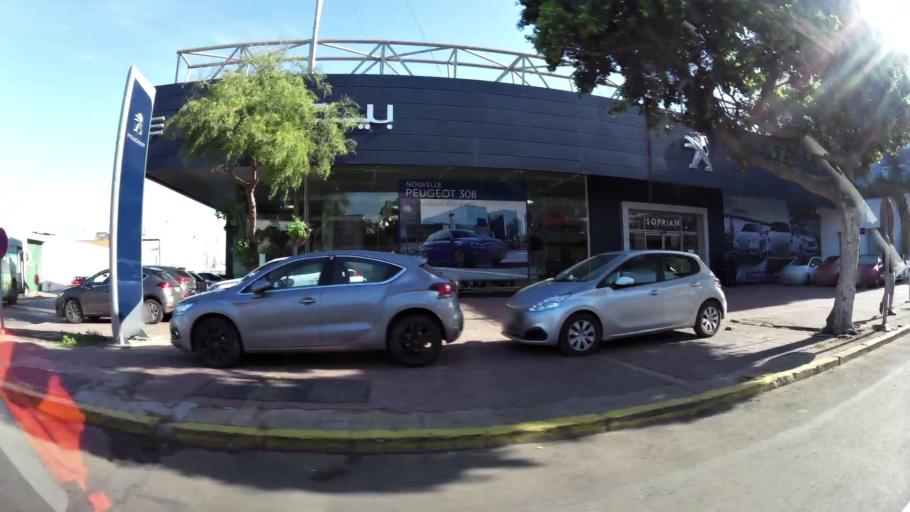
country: MA
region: Grand Casablanca
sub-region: Casablanca
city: Casablanca
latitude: 33.5966
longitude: -7.6058
